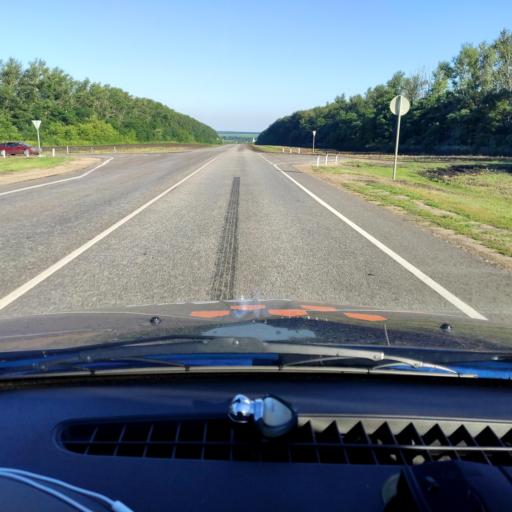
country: RU
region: Orjol
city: Zmiyevka
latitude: 52.6528
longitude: 36.5211
